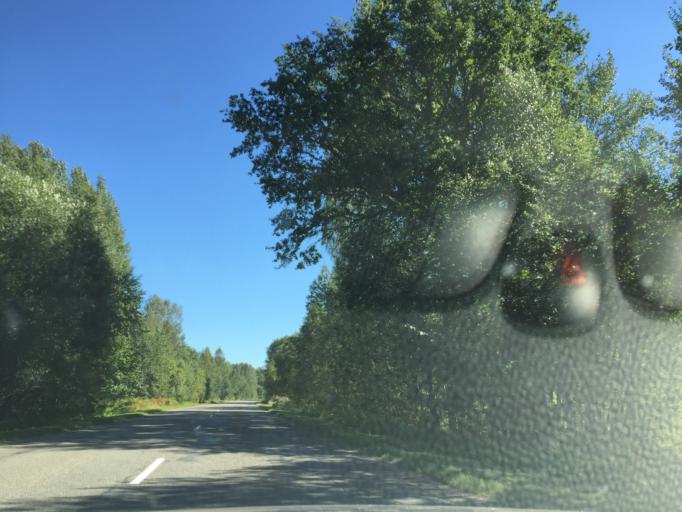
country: LV
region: Akniste
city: Akniste
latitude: 56.1395
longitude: 25.8139
